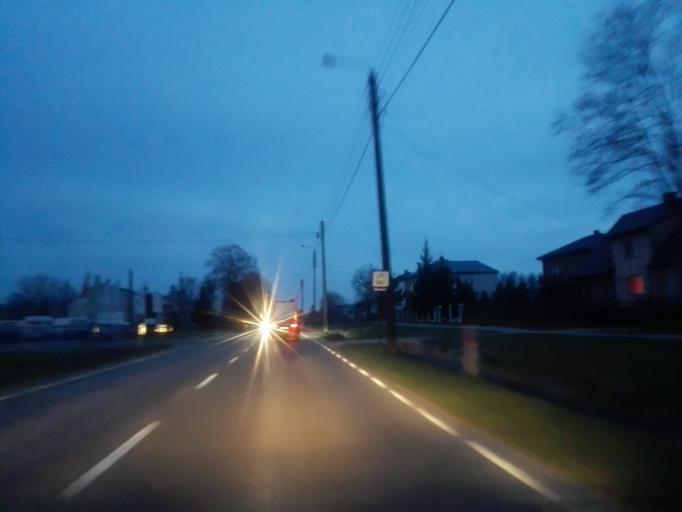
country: PL
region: Podlasie
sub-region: Lomza
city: Lomza
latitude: 53.1429
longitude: 22.0449
